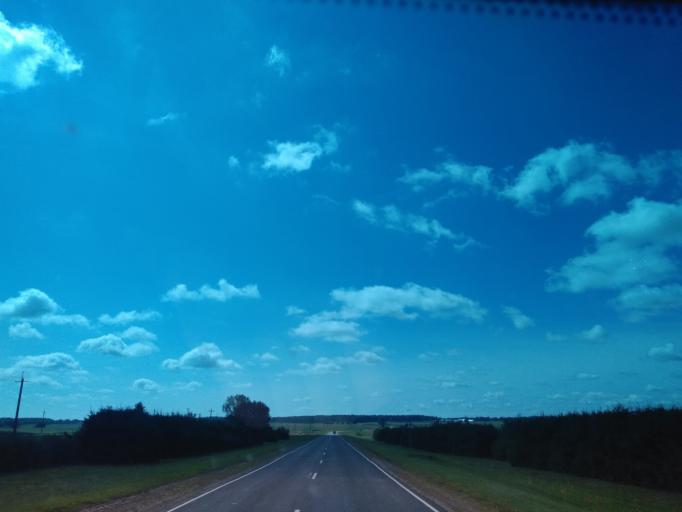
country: BY
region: Minsk
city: Uzda
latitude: 53.3725
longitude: 27.2343
